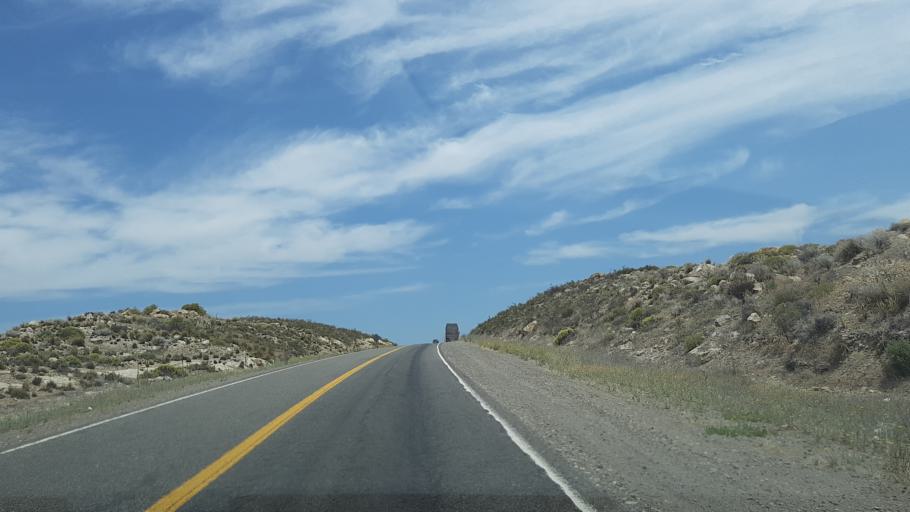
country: AR
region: Rio Negro
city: Pilcaniyeu
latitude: -40.5032
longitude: -70.6812
